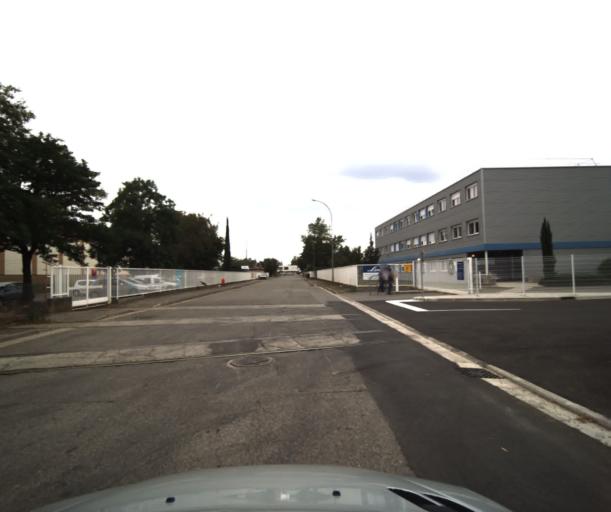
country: FR
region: Midi-Pyrenees
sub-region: Departement de la Haute-Garonne
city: Pinsaguel
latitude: 43.5301
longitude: 1.3784
